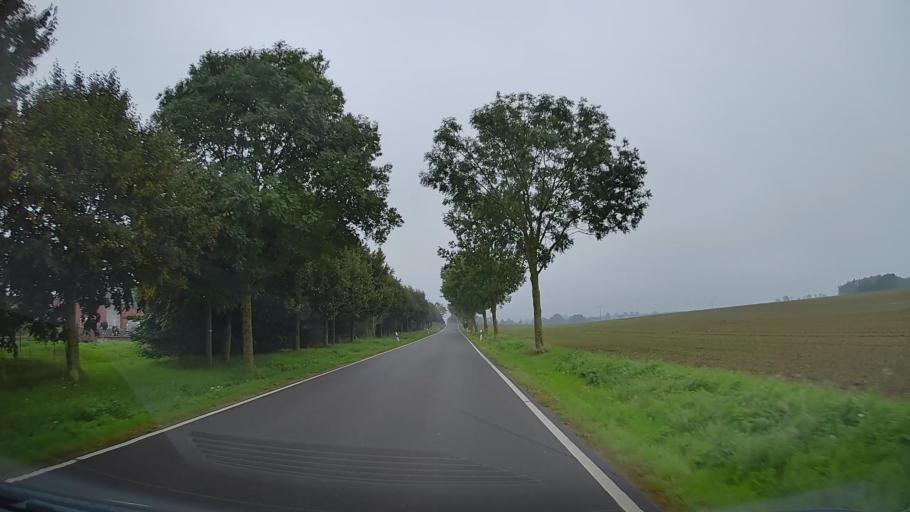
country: DE
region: Mecklenburg-Vorpommern
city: Gramkow
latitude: 53.9207
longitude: 11.3846
